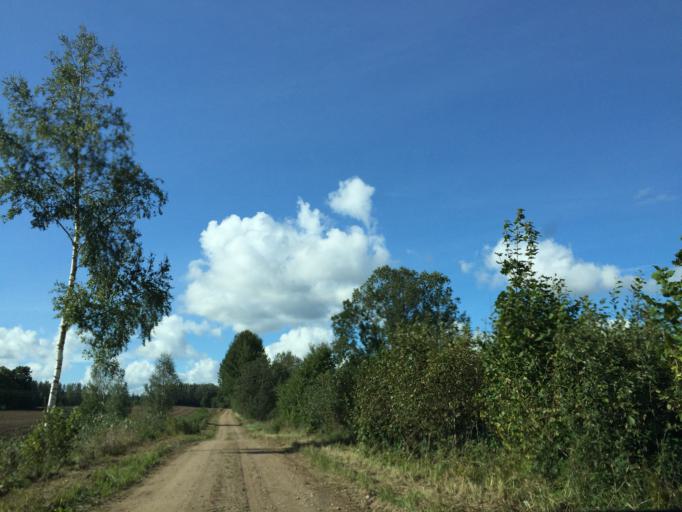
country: LV
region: Kuldigas Rajons
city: Kuldiga
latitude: 56.9951
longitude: 21.8270
